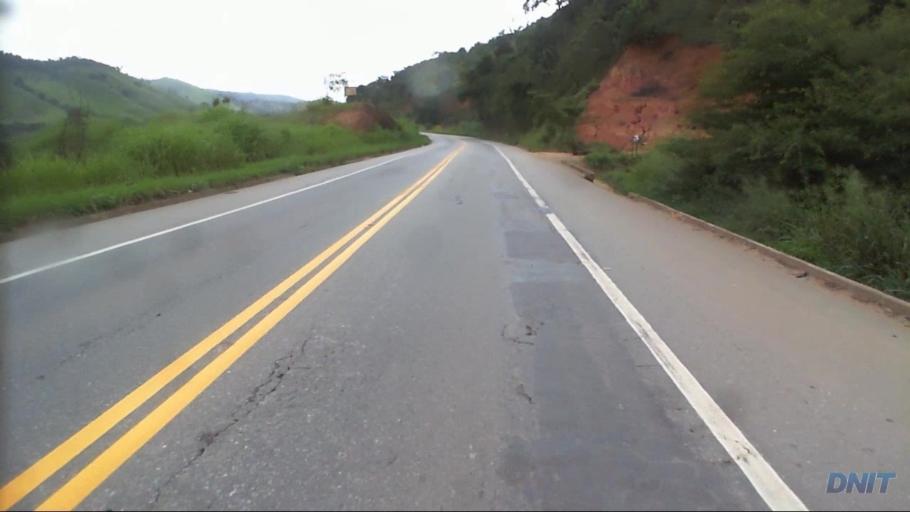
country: BR
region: Minas Gerais
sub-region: Nova Era
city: Nova Era
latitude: -19.7316
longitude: -43.0168
